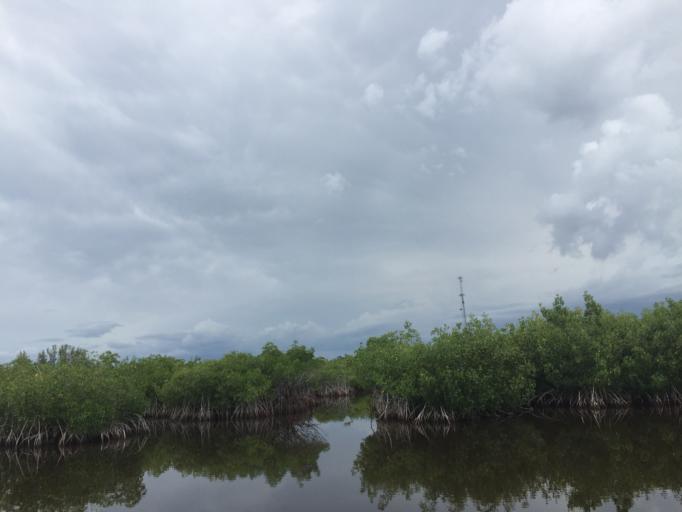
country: US
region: Florida
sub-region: Collier County
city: Marco
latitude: 25.9076
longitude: -81.3717
